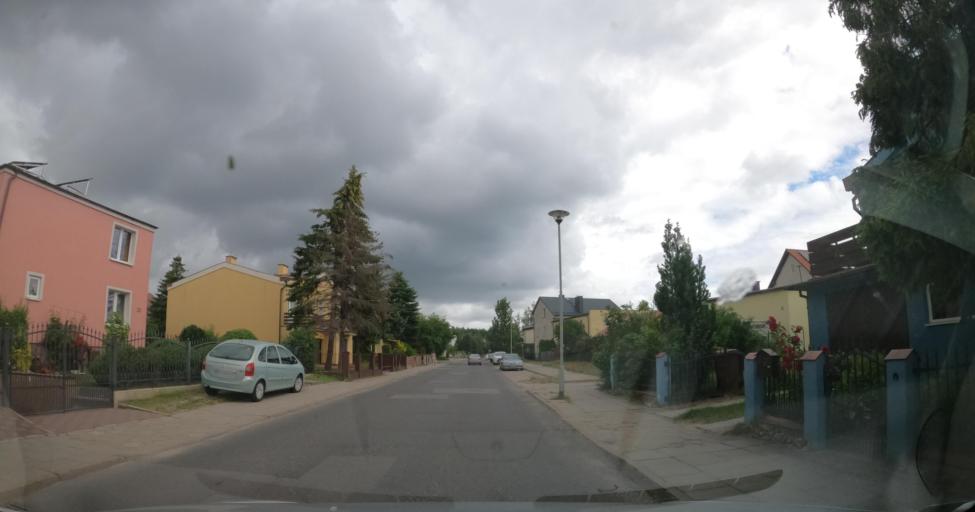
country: PL
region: Pomeranian Voivodeship
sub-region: Gdynia
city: Wielki Kack
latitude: 54.4274
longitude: 18.4728
